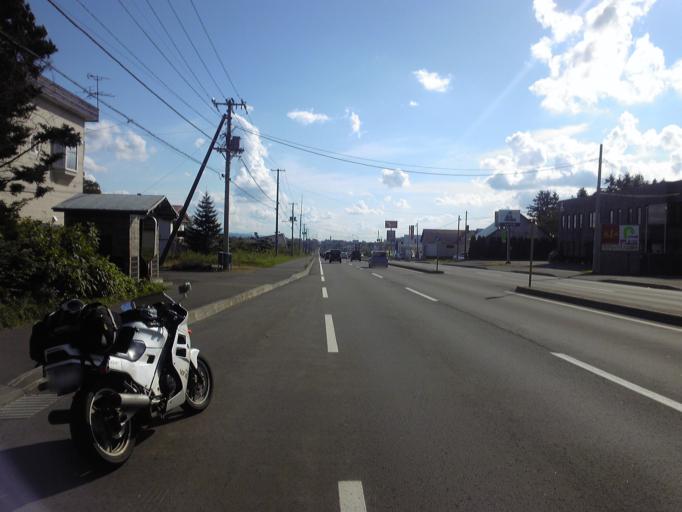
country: JP
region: Hokkaido
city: Sunagawa
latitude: 43.5108
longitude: 141.9129
